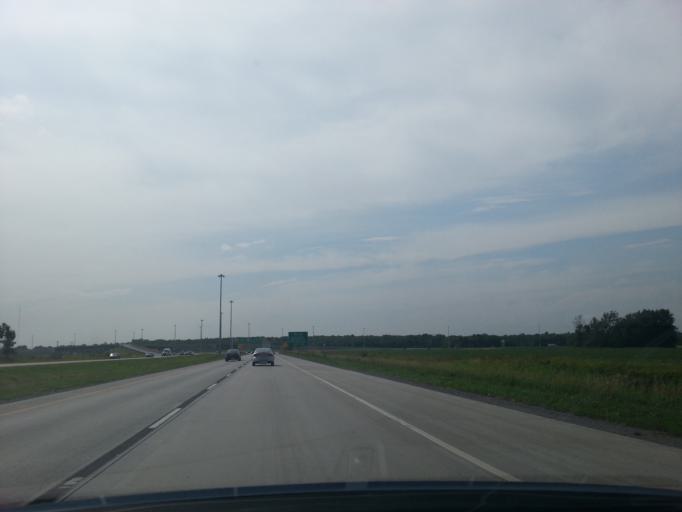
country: CA
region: Quebec
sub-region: Monteregie
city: Saint-Constant
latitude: 45.3679
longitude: -73.6122
